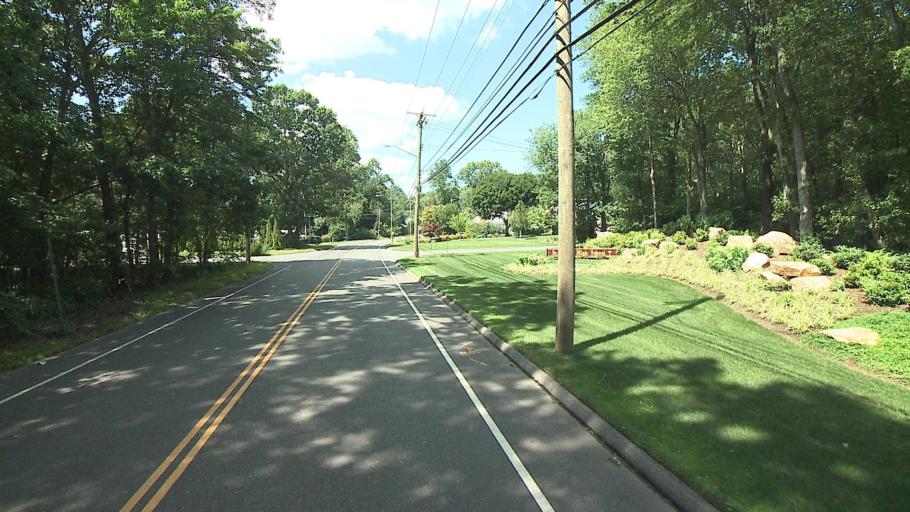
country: US
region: Connecticut
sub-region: Fairfield County
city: Trumbull
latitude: 41.2616
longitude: -73.1668
